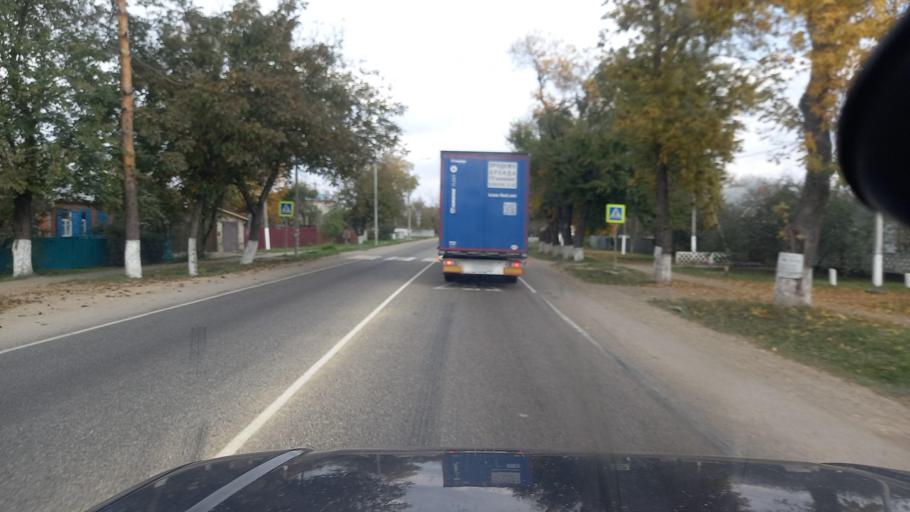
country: RU
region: Krasnodarskiy
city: Kholmskiy
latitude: 44.8483
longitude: 38.3964
